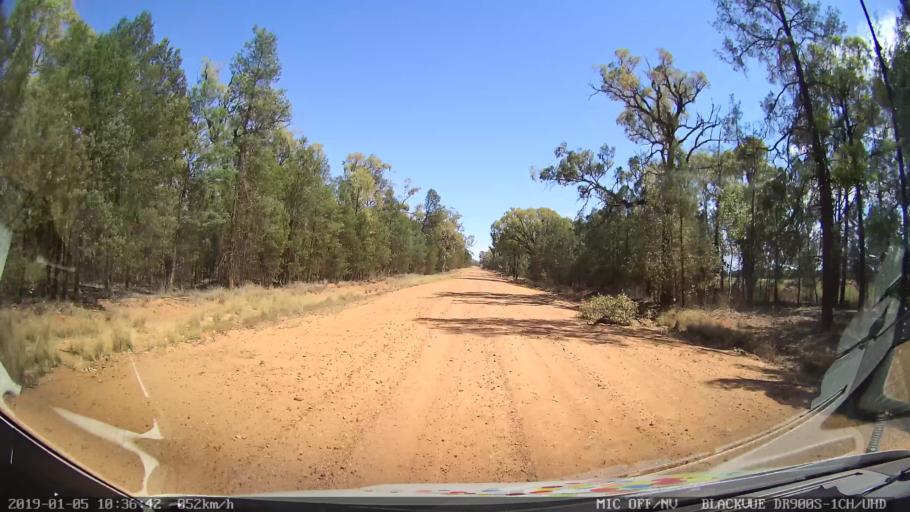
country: AU
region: New South Wales
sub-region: Gilgandra
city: Gilgandra
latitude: -31.4800
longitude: 148.9241
